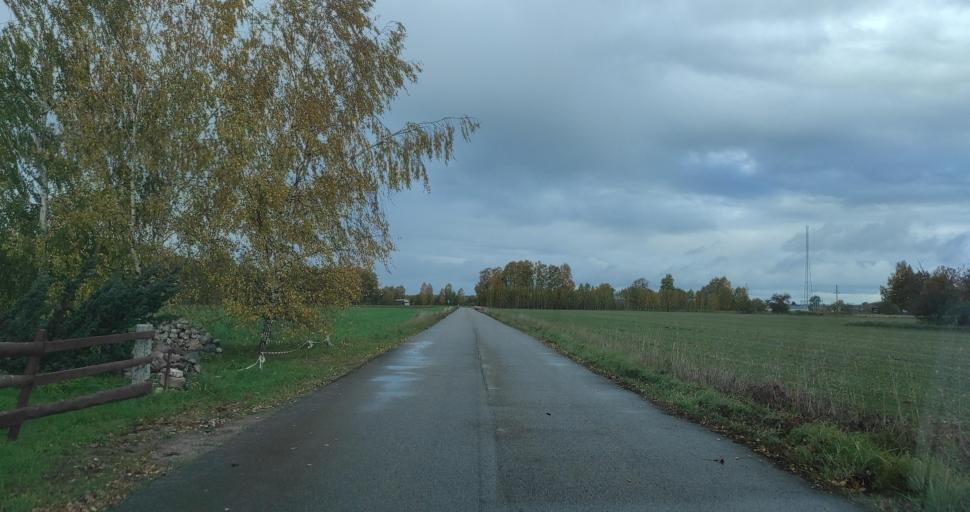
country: LV
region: Skrunda
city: Skrunda
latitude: 56.6895
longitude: 22.0198
